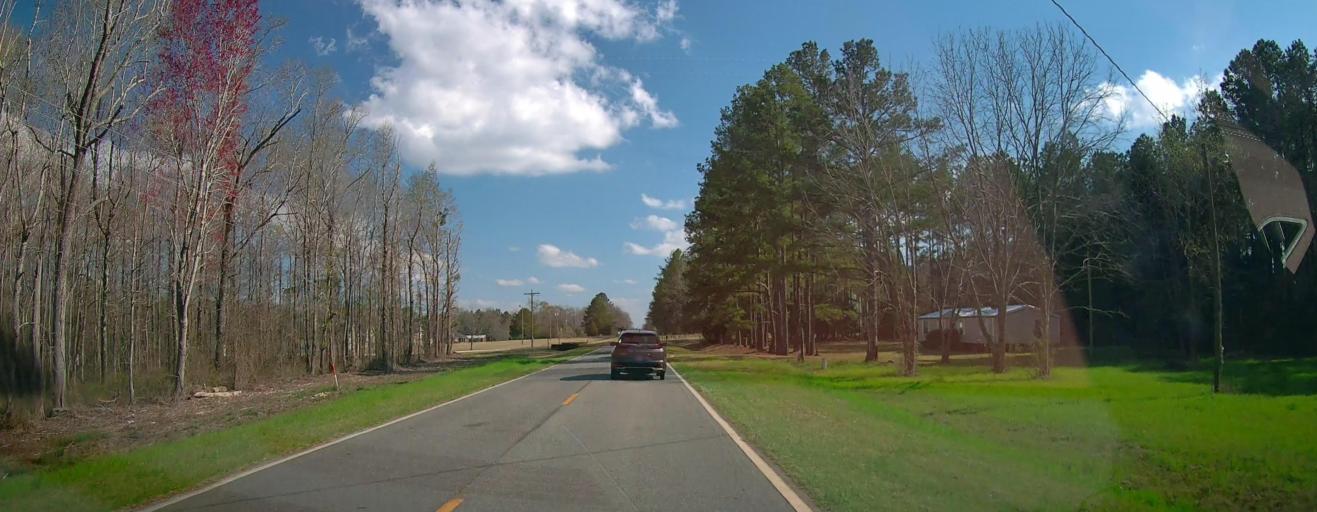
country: US
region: Georgia
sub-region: Laurens County
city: Dublin
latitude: 32.6142
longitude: -83.0832
